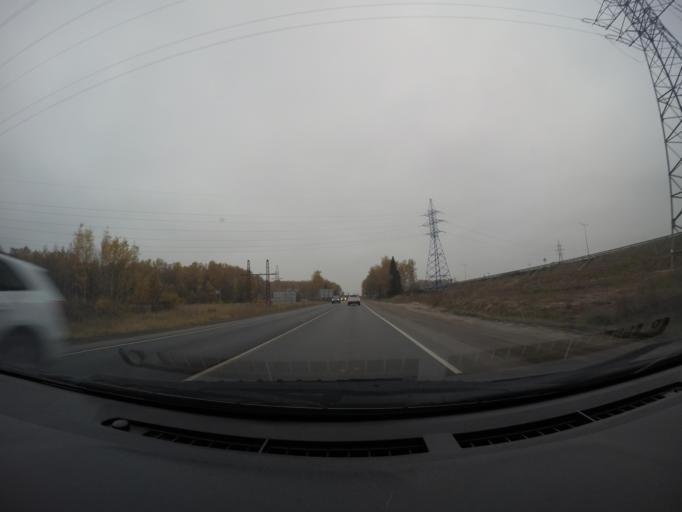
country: RU
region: Moskovskaya
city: Belyye Stolby
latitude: 55.3375
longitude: 37.7937
